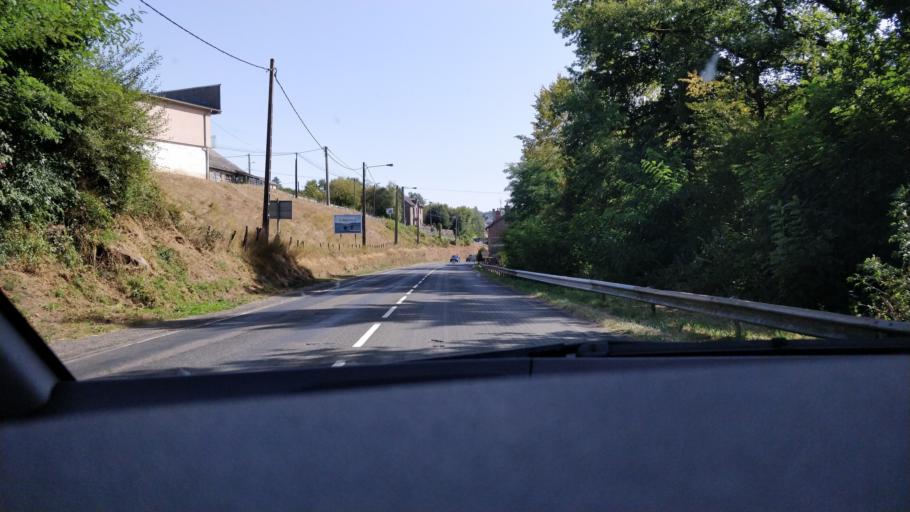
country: FR
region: Limousin
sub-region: Departement de la Correze
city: Uzerche
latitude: 45.4372
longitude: 1.5636
